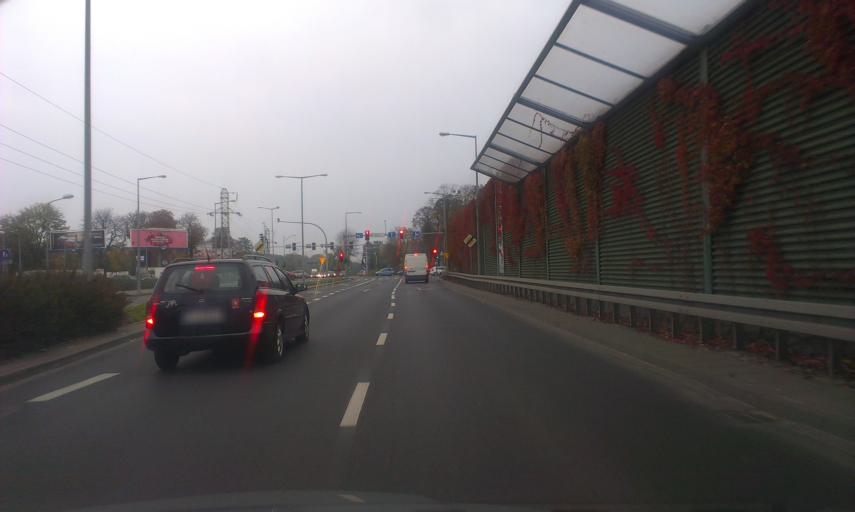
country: PL
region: Greater Poland Voivodeship
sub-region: Poznan
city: Poznan
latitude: 52.4111
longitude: 16.8693
